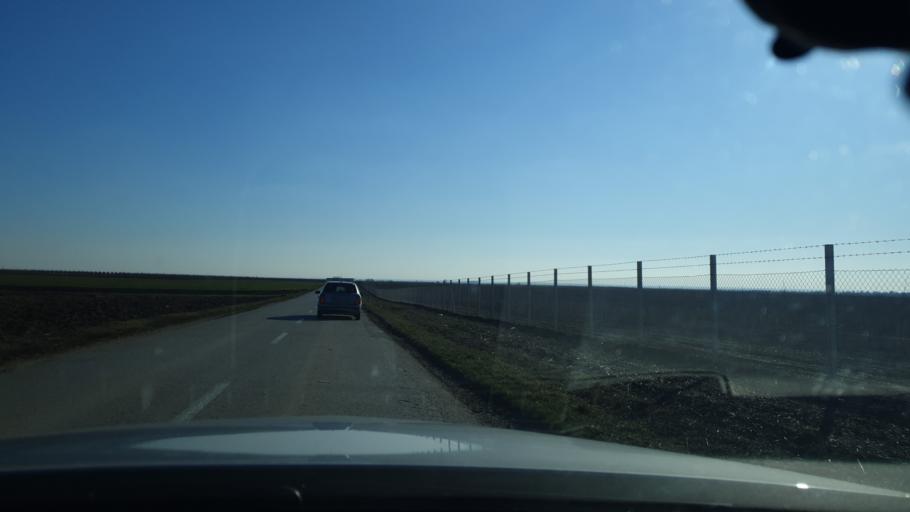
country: RS
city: Vrdnik
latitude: 45.0684
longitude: 19.8089
